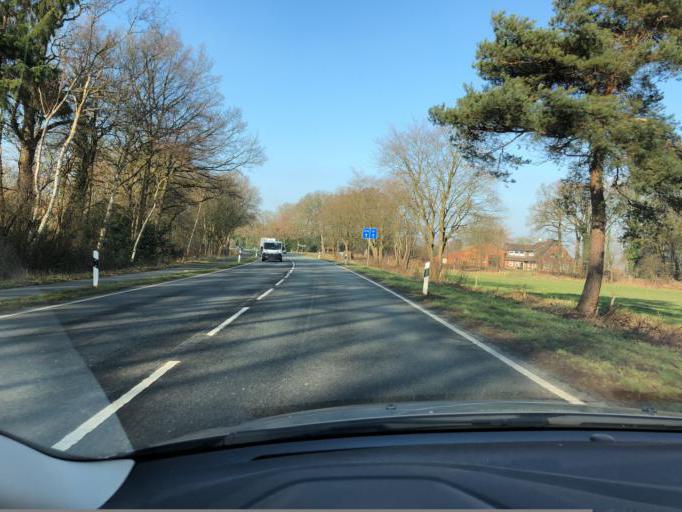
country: DE
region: Lower Saxony
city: Westerstede
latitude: 53.2902
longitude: 7.8878
